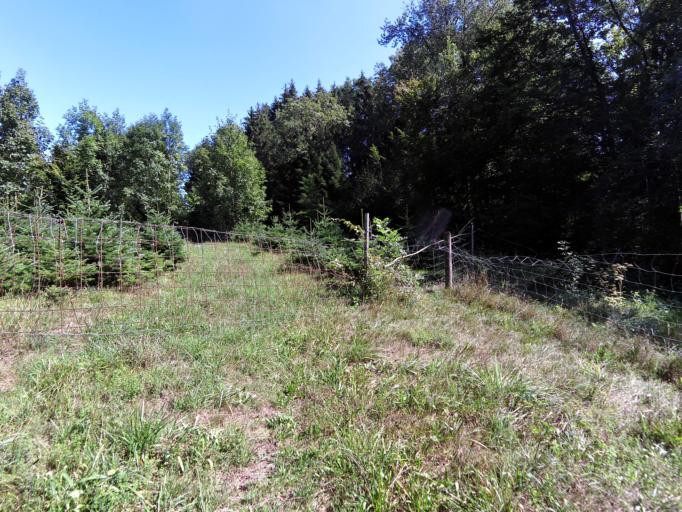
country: CH
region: Thurgau
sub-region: Weinfelden District
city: Wigoltingen
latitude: 47.6229
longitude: 9.0370
